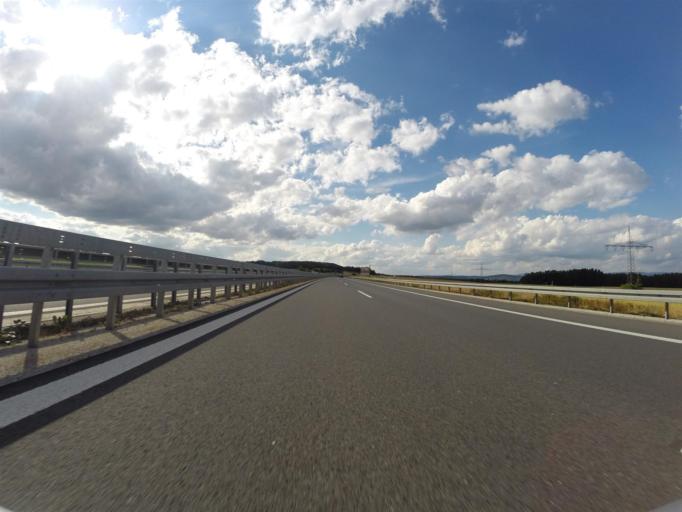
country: DE
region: Bavaria
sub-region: Upper Franconia
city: Rodental
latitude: 50.2543
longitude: 11.0259
